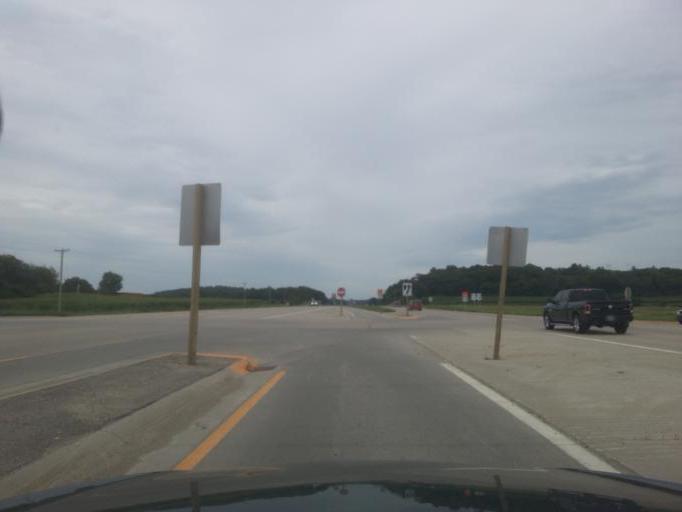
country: US
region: Wisconsin
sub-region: Dane County
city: McFarland
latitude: 43.0407
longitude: -89.2474
